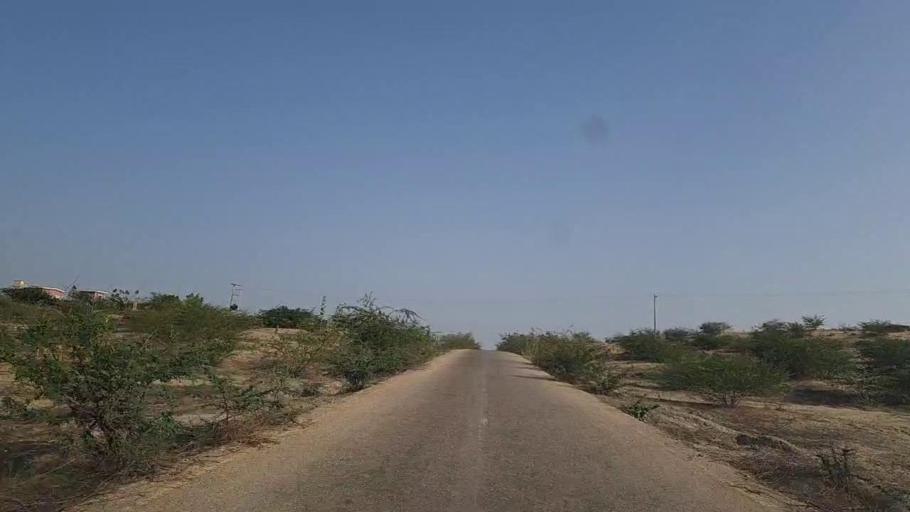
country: PK
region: Sindh
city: Naukot
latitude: 24.6248
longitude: 69.3679
